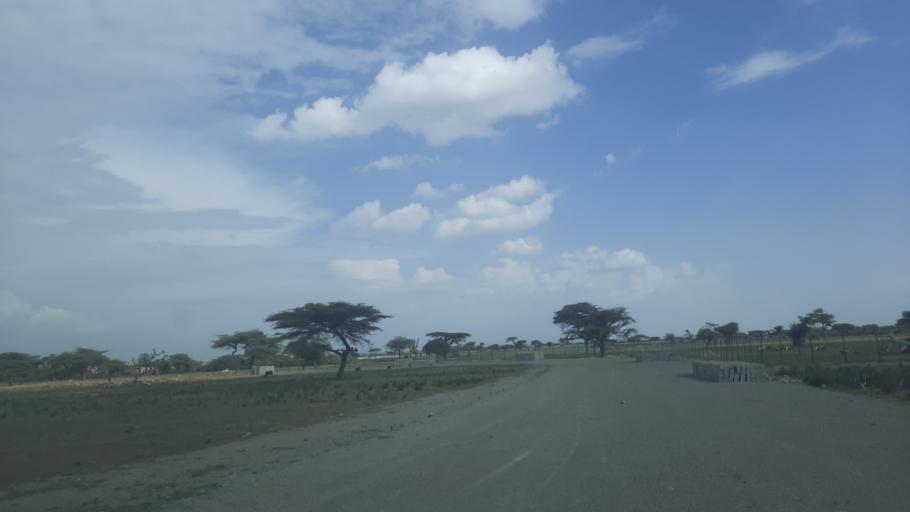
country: ET
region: Oromiya
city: Ziway
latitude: 7.6983
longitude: 38.6556
